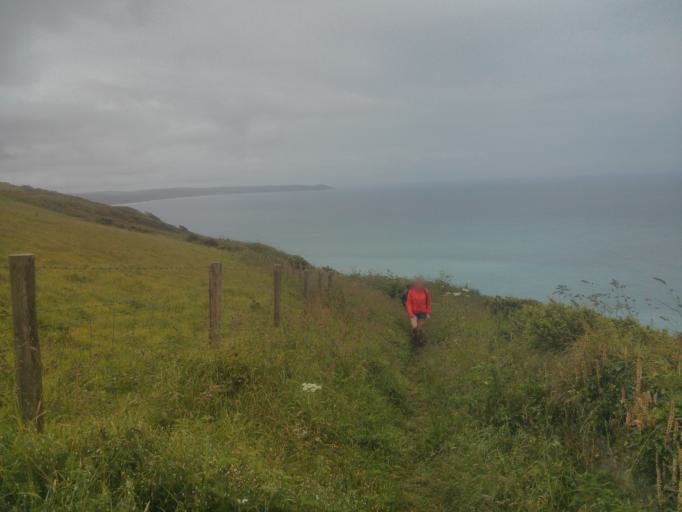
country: GB
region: England
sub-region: Cornwall
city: Pillaton
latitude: 50.3628
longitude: -4.3521
